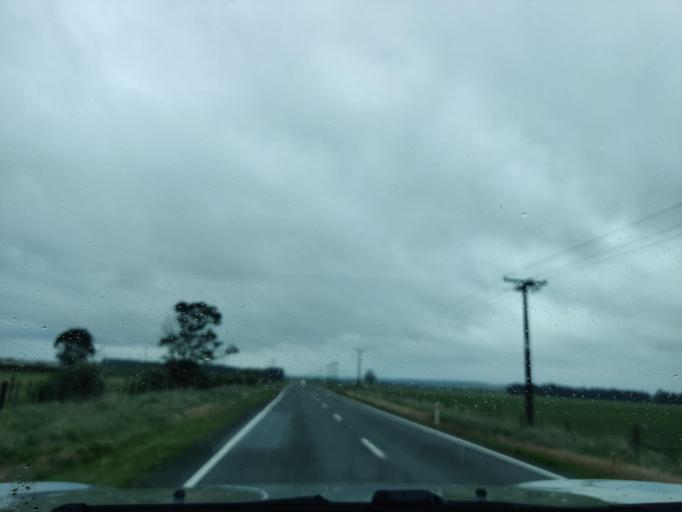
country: NZ
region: Hawke's Bay
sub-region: Hastings District
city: Hastings
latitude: -40.0114
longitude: 176.3727
